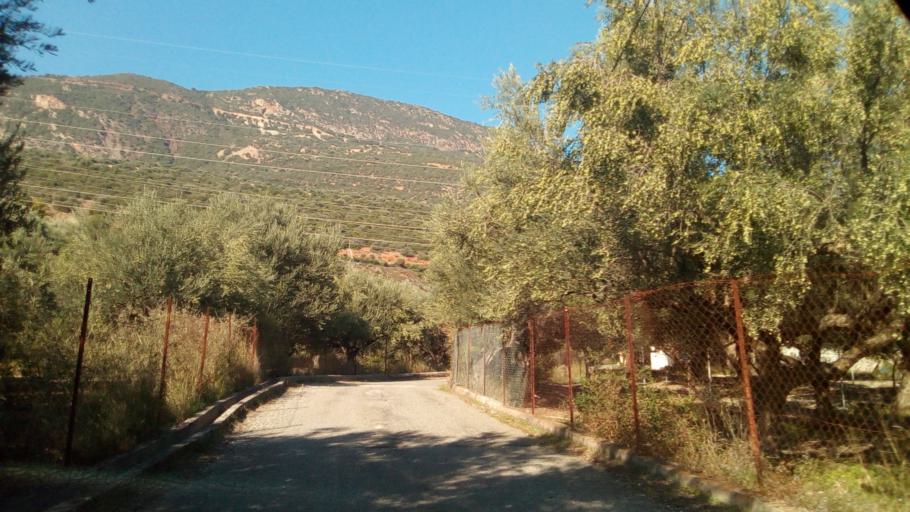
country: GR
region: West Greece
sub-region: Nomos Achaias
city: Selianitika
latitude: 38.3848
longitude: 22.0789
